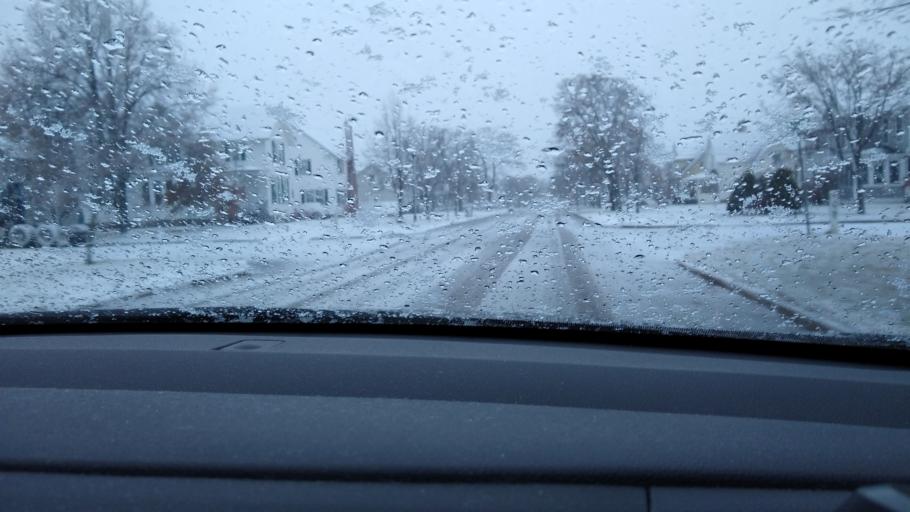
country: US
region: Michigan
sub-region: Delta County
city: Escanaba
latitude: 45.7396
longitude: -87.0594
